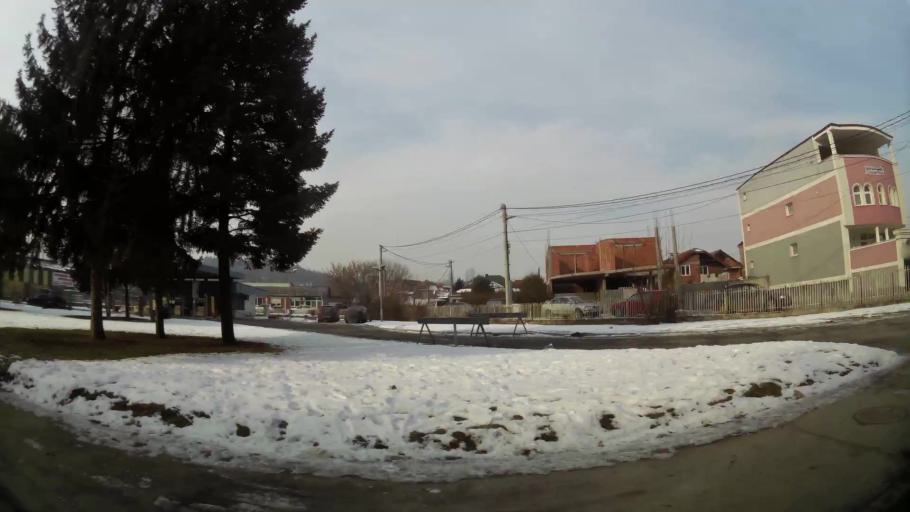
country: MK
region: Cair
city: Cair
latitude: 42.0180
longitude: 21.4309
